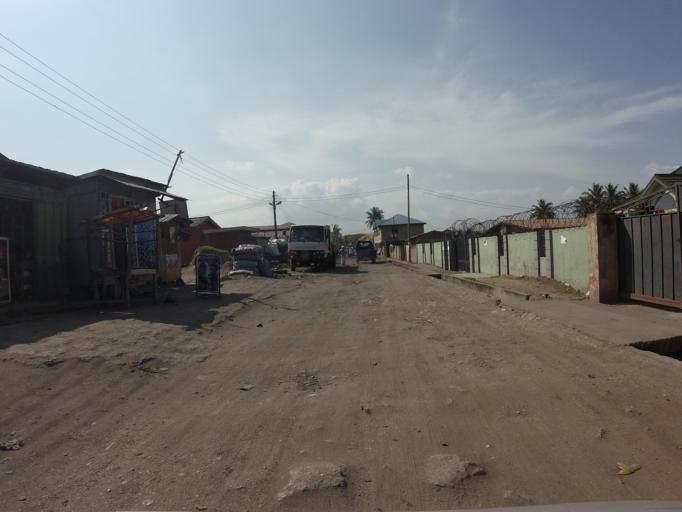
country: GH
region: Greater Accra
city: Dome
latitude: 5.6434
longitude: -0.2353
